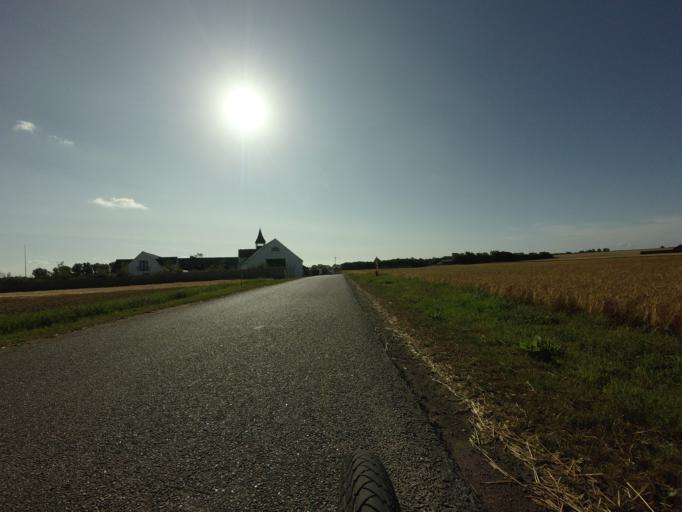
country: DK
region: North Denmark
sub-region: Hjorring Kommune
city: Vra
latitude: 57.3845
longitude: 9.9921
